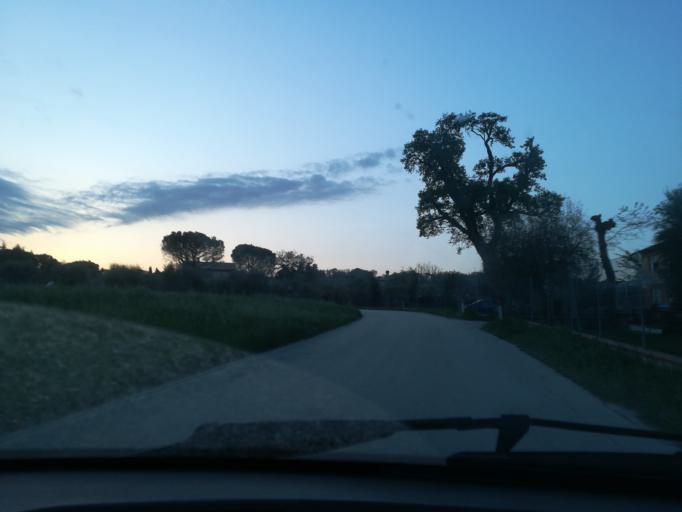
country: IT
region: The Marches
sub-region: Provincia di Macerata
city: Macerata
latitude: 43.2738
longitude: 13.4562
